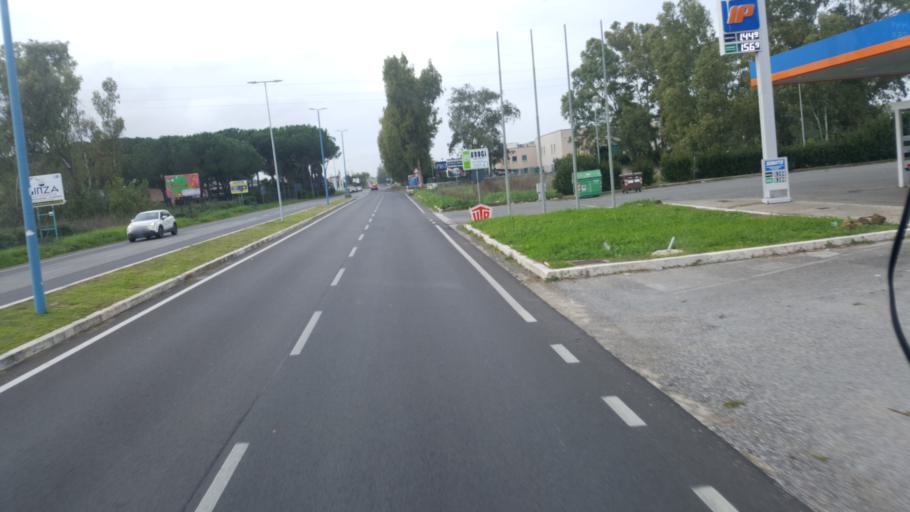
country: IT
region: Latium
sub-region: Provincia di Latina
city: Latina
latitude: 41.4787
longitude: 12.8726
